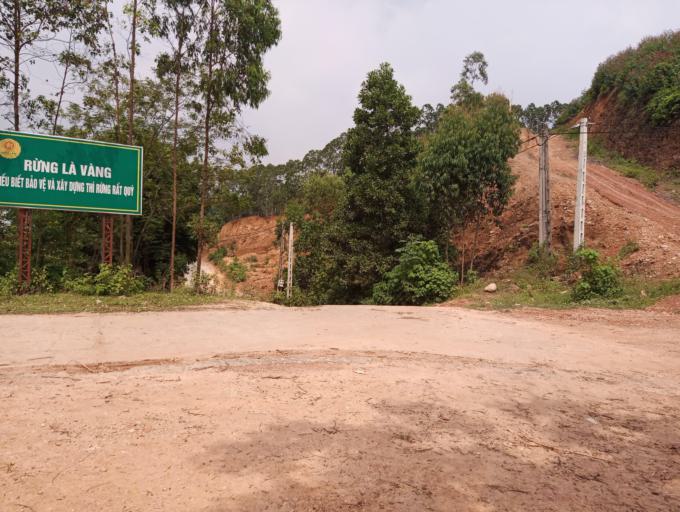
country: VN
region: Vinh Phuc
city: Huong Canh
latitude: 21.3569
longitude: 105.7054
